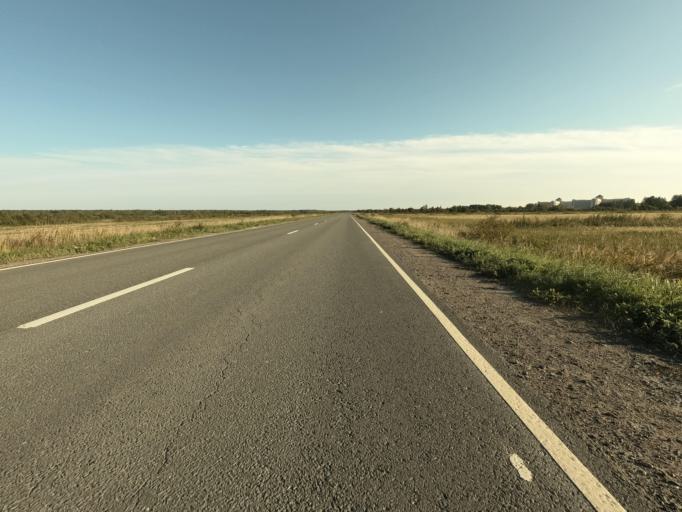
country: RU
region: St.-Petersburg
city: Sapernyy
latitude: 59.7530
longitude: 30.6347
